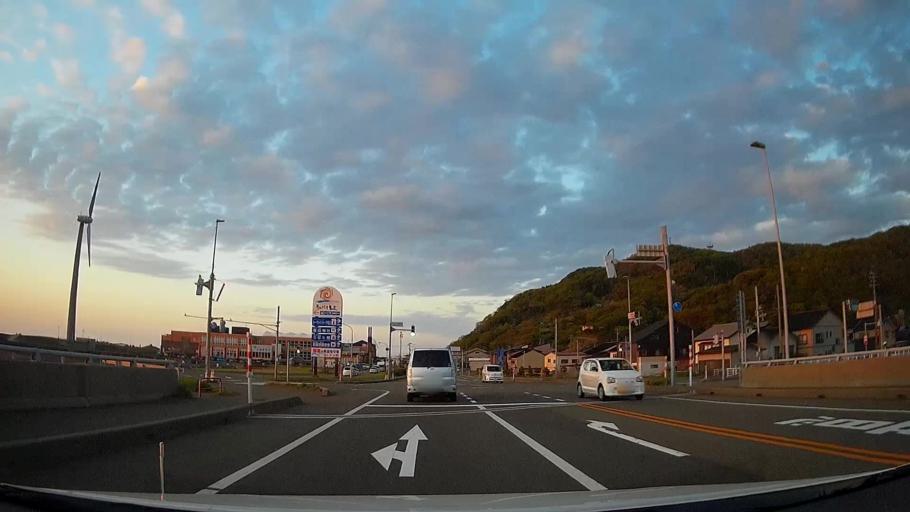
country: JP
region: Niigata
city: Joetsu
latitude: 37.1608
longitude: 138.0854
